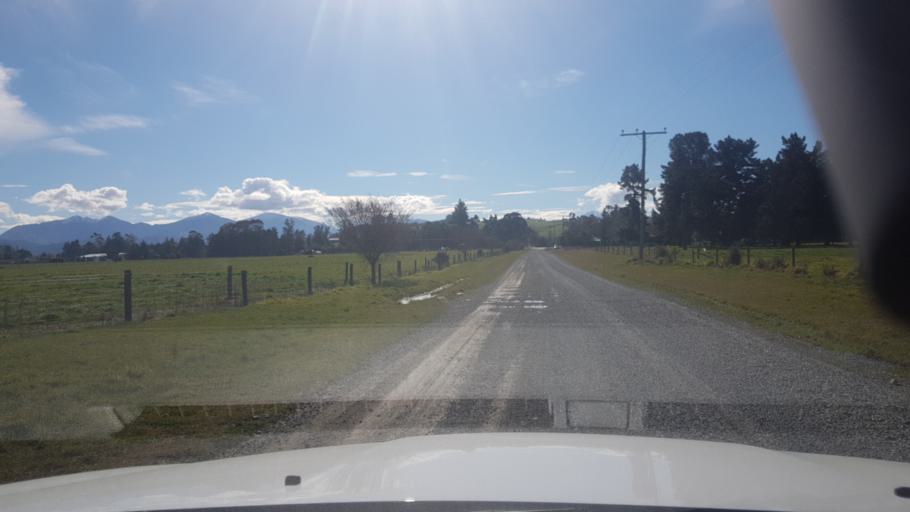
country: NZ
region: Canterbury
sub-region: Timaru District
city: Pleasant Point
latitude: -44.1165
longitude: 171.2256
